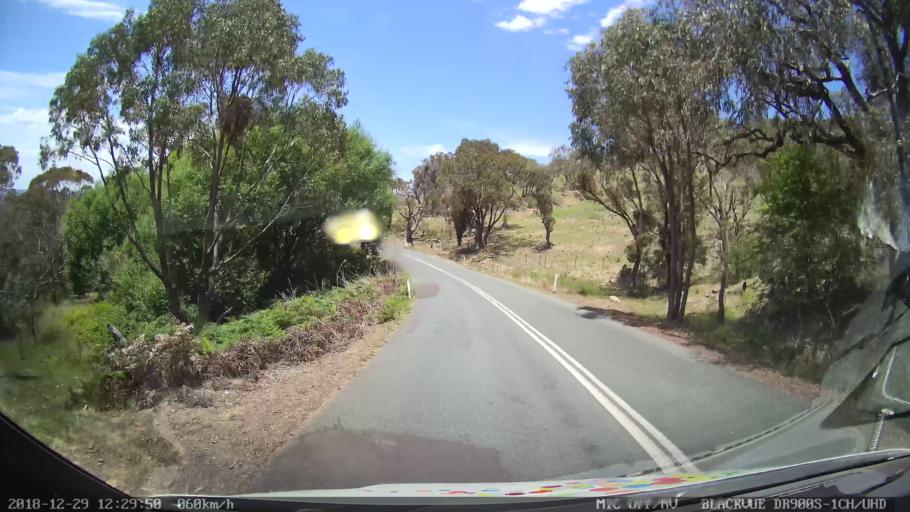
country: AU
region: Australian Capital Territory
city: Macarthur
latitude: -35.5013
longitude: 149.2317
